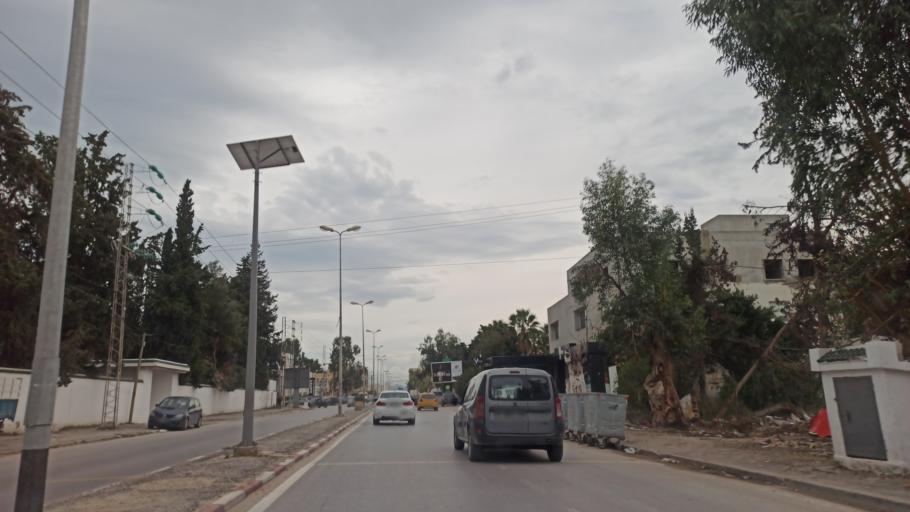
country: TN
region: Ariana
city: Ariana
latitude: 36.8693
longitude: 10.2494
